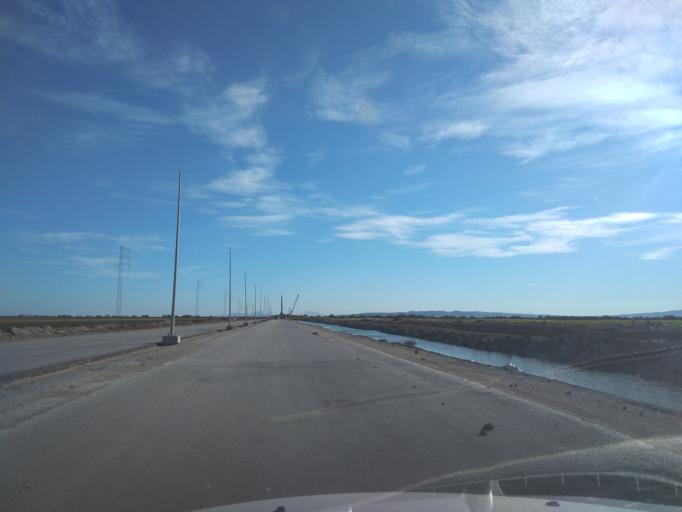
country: TN
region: Ariana
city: Qal'at al Andalus
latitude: 37.0290
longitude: 10.1374
